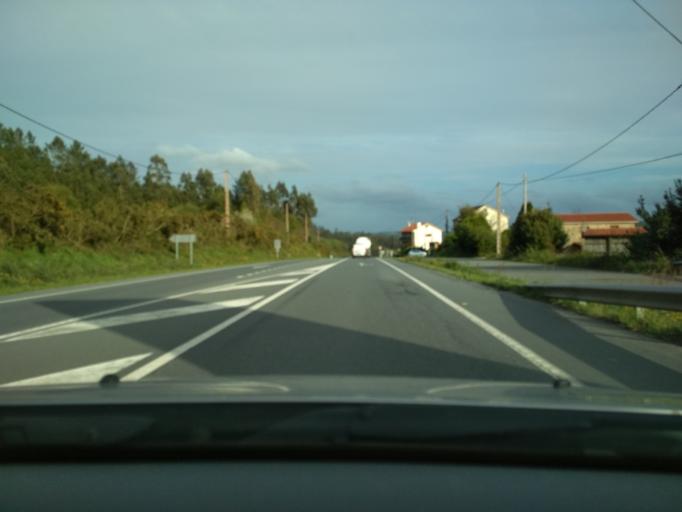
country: ES
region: Galicia
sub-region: Provincia da Coruna
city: Cerceda
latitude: 43.2279
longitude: -8.4658
